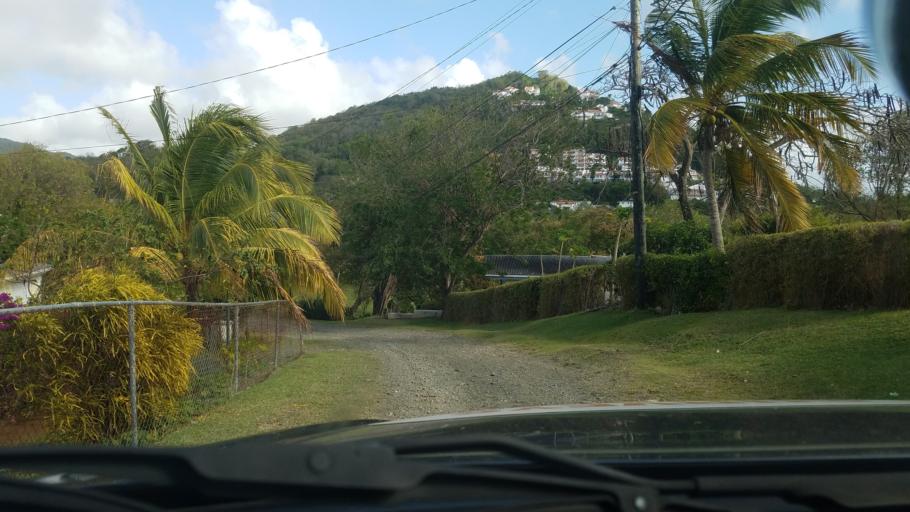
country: LC
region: Gros-Islet
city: Gros Islet
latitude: 14.0641
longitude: -60.9735
